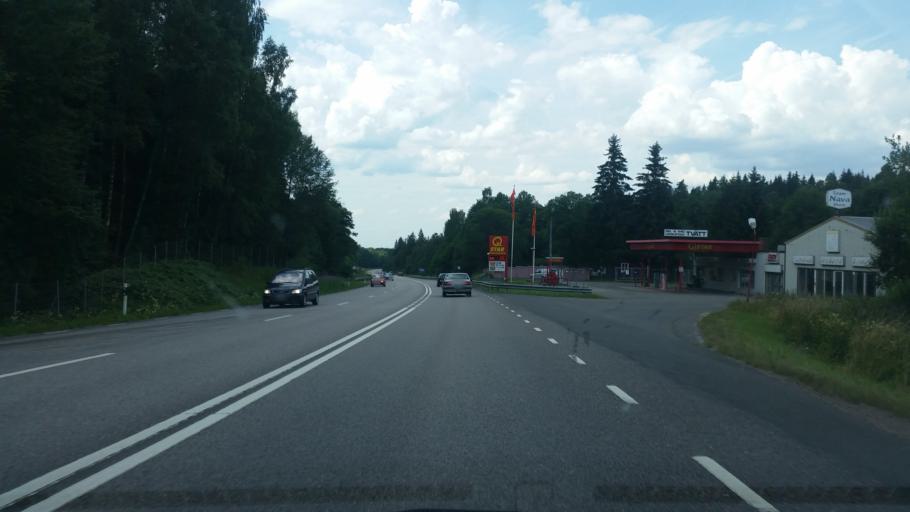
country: SE
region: Vaestra Goetaland
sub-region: Skovde Kommun
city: Skultorp
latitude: 58.3788
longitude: 13.7016
